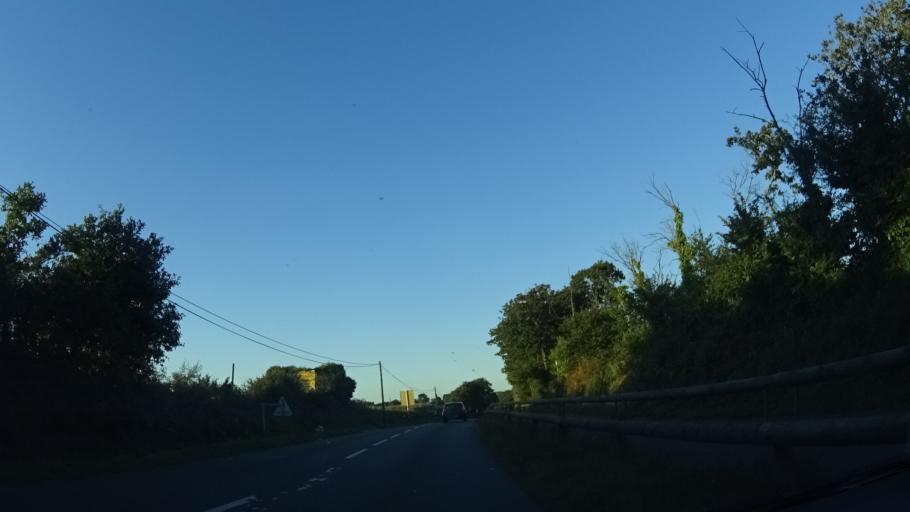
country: FR
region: Brittany
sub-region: Departement du Finistere
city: Guilers
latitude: 48.4127
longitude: -4.5608
